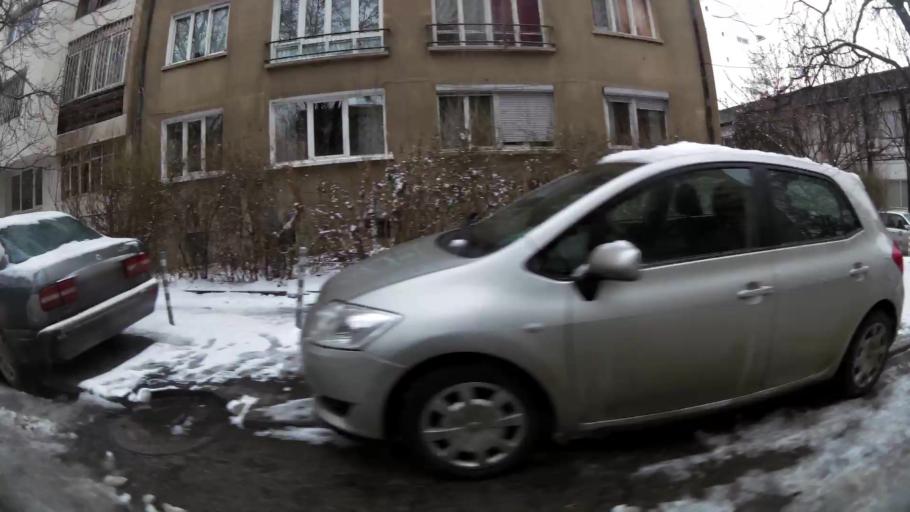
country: BG
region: Sofia-Capital
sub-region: Stolichna Obshtina
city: Sofia
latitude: 42.6921
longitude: 23.3519
